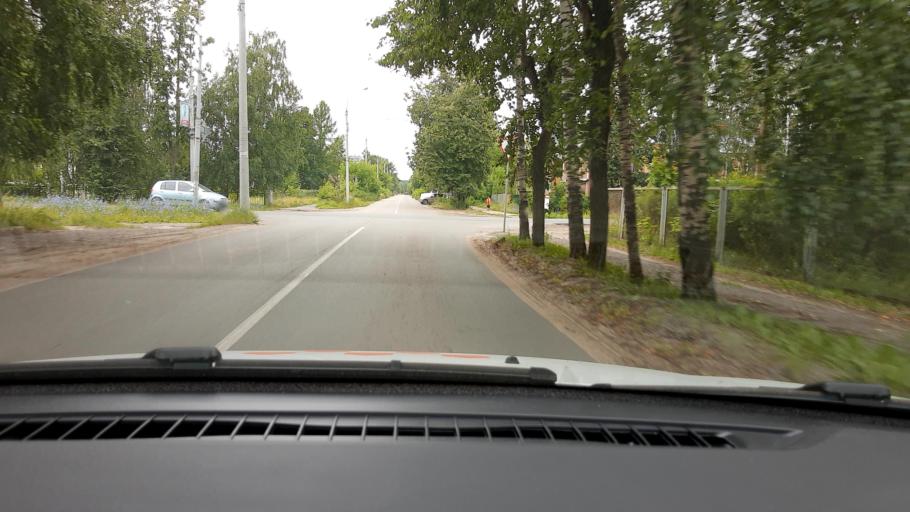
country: RU
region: Nizjnij Novgorod
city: Pyra
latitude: 56.2525
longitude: 43.3918
